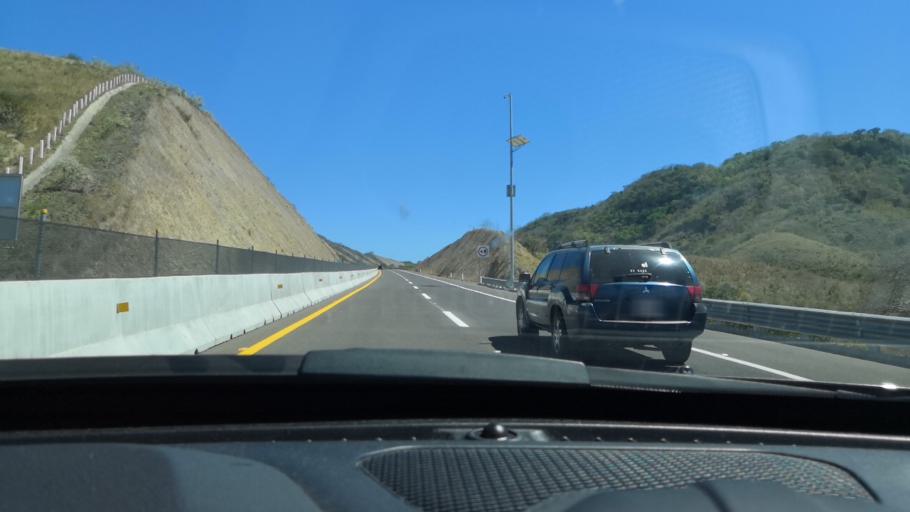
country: MX
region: Nayarit
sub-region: Compostela
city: Juan Escutia (Borbollon)
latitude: 21.1330
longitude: -104.9074
